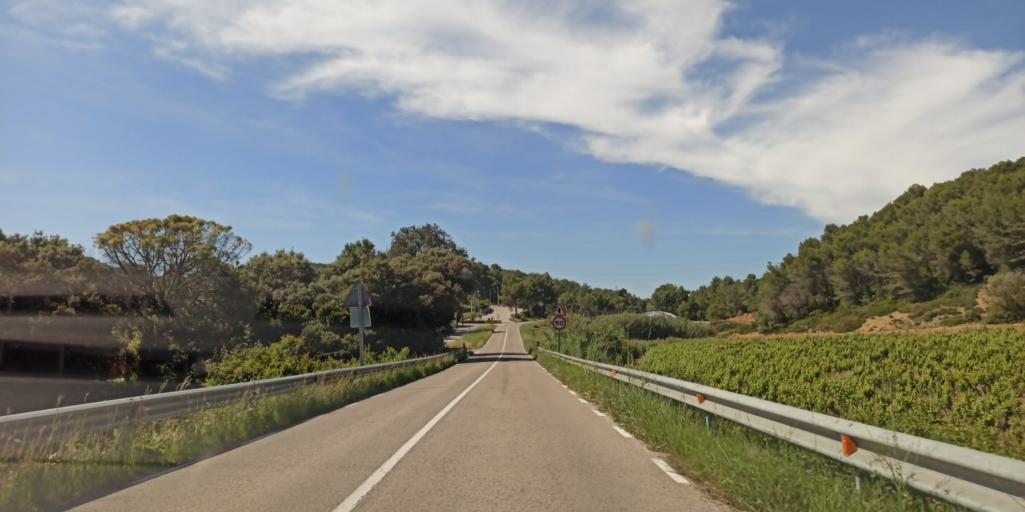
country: ES
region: Catalonia
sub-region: Provincia de Barcelona
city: Avinyonet del Penedes
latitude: 41.3173
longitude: 1.7586
